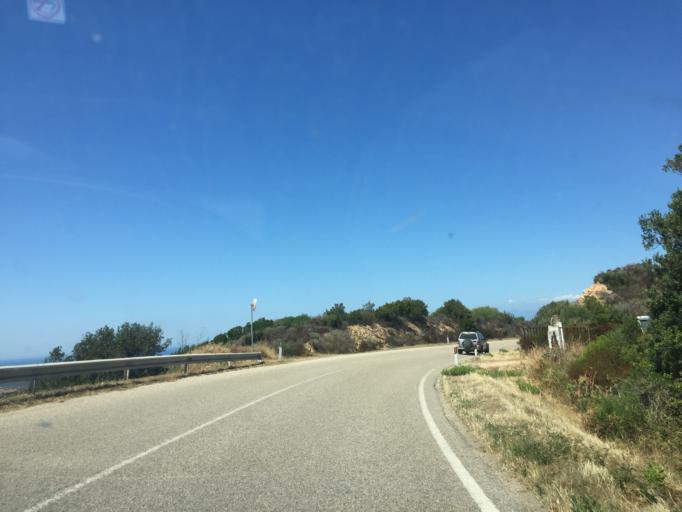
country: IT
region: Sardinia
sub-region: Provincia di Olbia-Tempio
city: Aglientu
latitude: 41.0931
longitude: 9.0966
